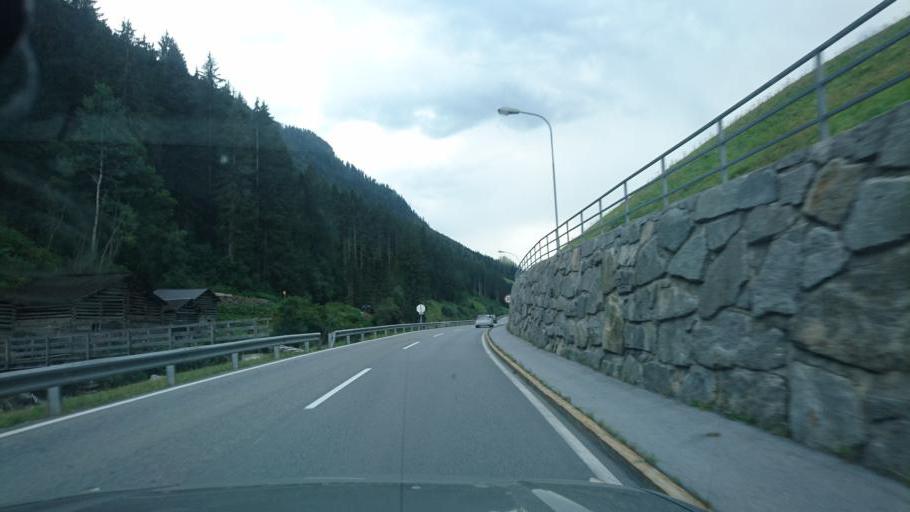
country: AT
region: Tyrol
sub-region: Politischer Bezirk Landeck
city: Kappl
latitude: 47.0552
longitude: 10.3634
